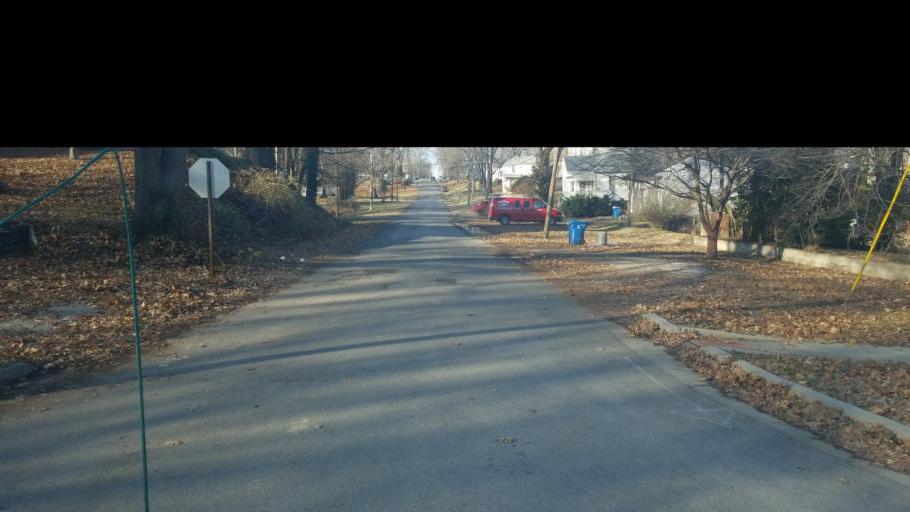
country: US
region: Illinois
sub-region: Wabash County
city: Mount Carmel
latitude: 38.4131
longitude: -87.7554
